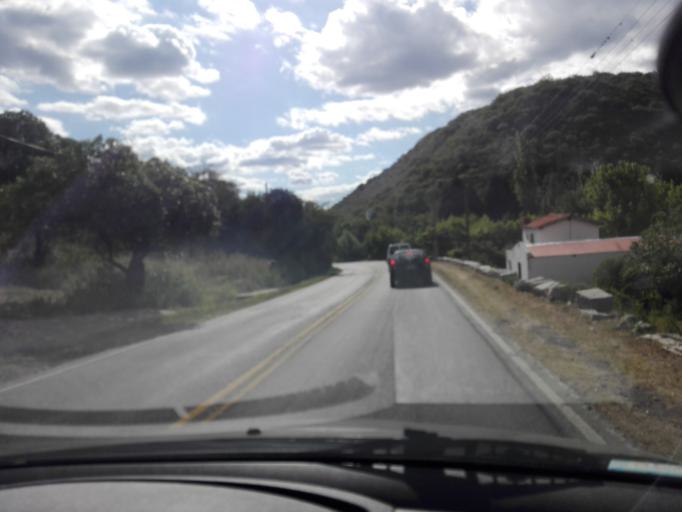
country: AR
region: Cordoba
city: Villa Las Rosas
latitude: -31.9088
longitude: -64.9982
